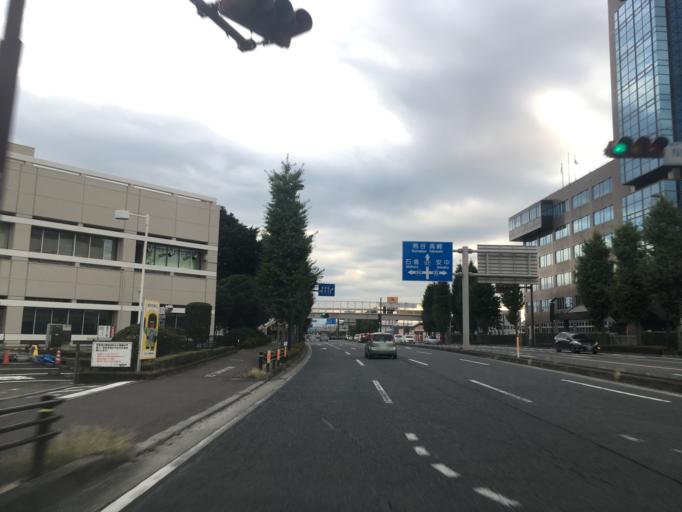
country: JP
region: Gunma
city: Maebashi-shi
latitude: 36.3853
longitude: 139.0456
